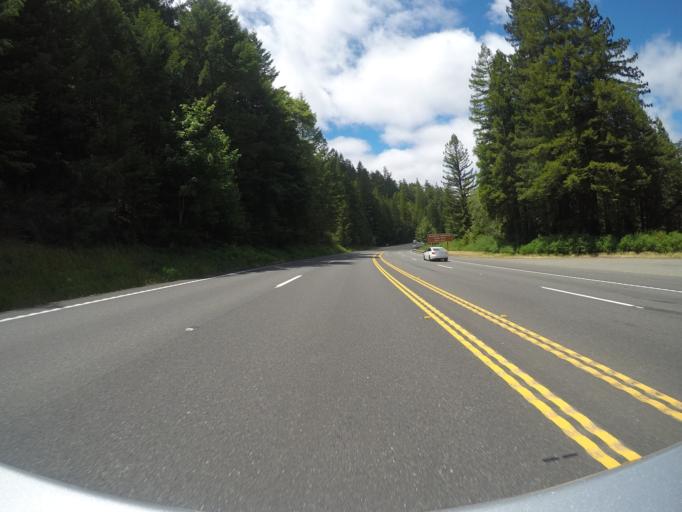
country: US
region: California
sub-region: Humboldt County
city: Redway
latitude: 40.2669
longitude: -123.8508
